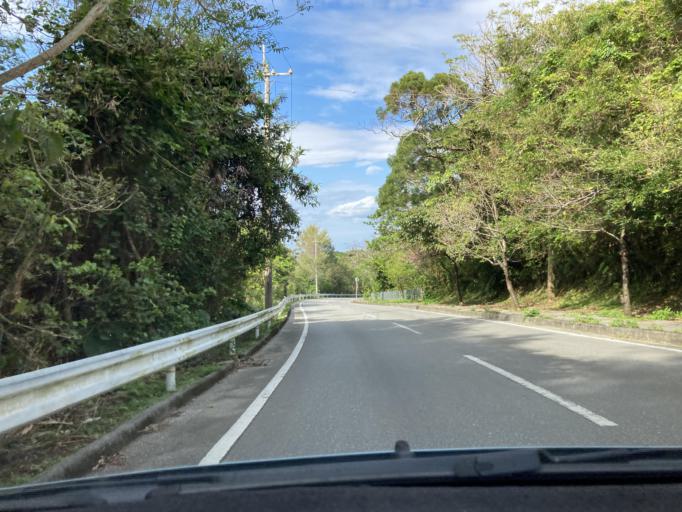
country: JP
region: Okinawa
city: Nago
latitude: 26.6970
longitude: 127.9248
